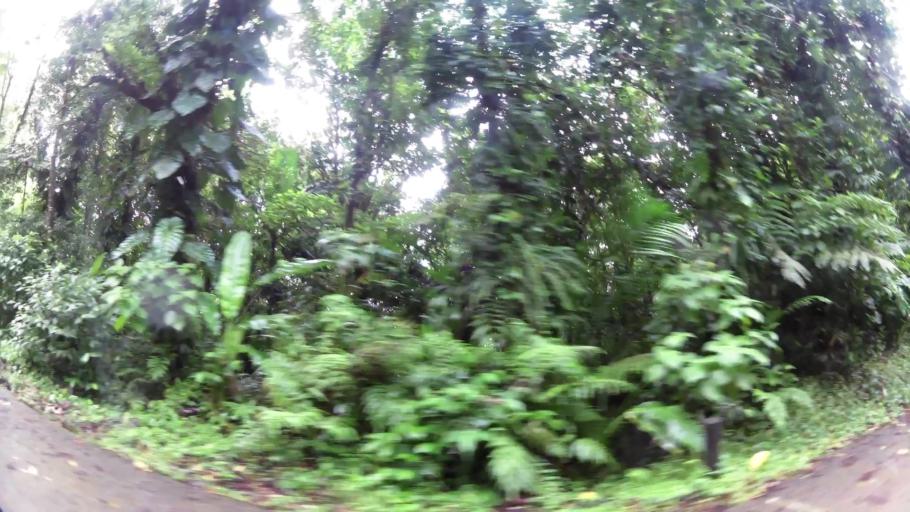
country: GP
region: Guadeloupe
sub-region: Guadeloupe
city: Trois-Rivieres
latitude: 16.0390
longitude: -61.6380
